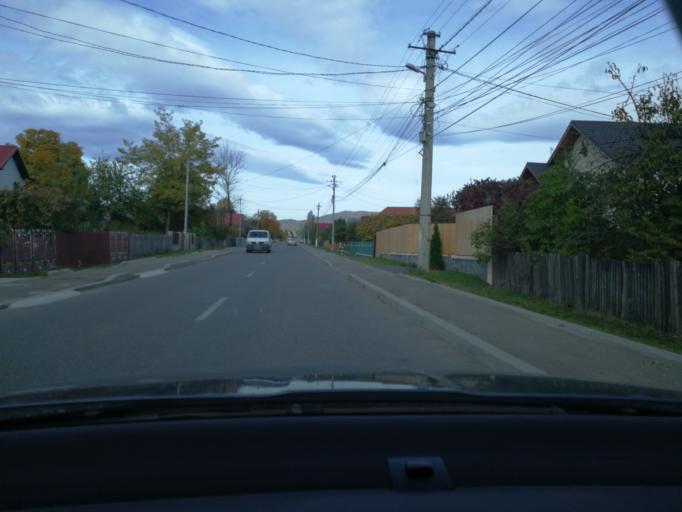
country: RO
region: Prahova
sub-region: Comuna Brebu
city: Brebu Megiesesc
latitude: 45.1727
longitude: 25.7710
